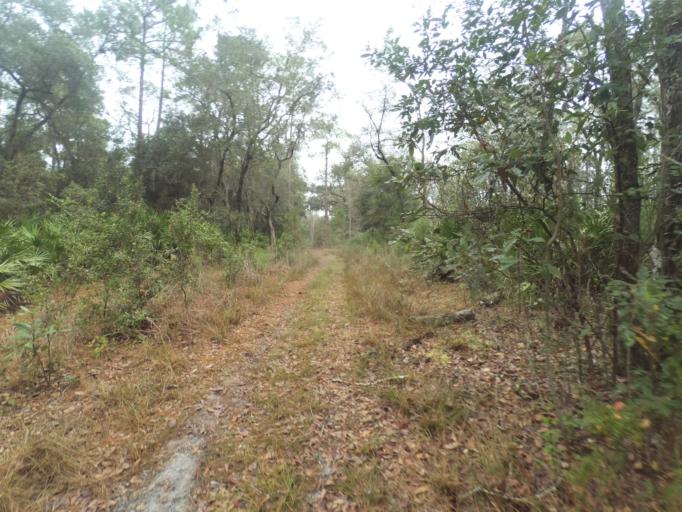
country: US
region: Florida
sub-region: Alachua County
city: Gainesville
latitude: 29.5398
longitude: -82.2724
